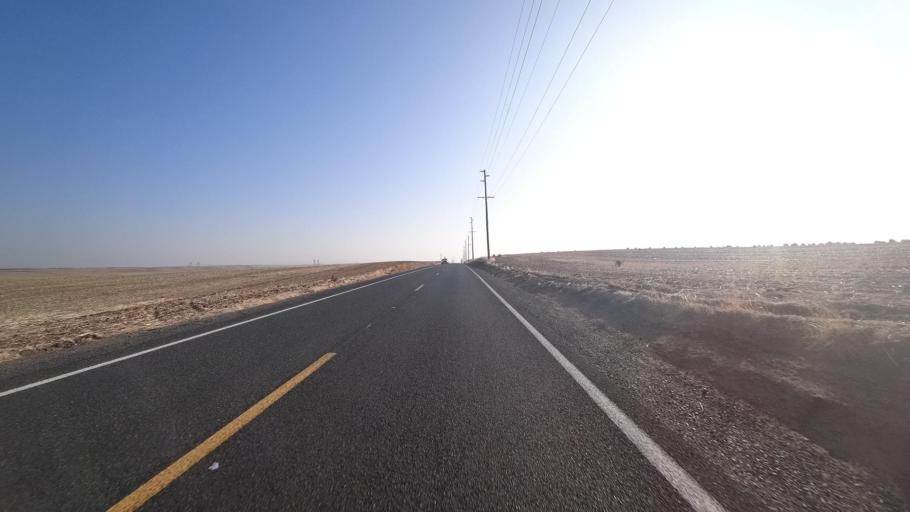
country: US
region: California
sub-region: Tulare County
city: Richgrove
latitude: 35.7619
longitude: -119.0712
